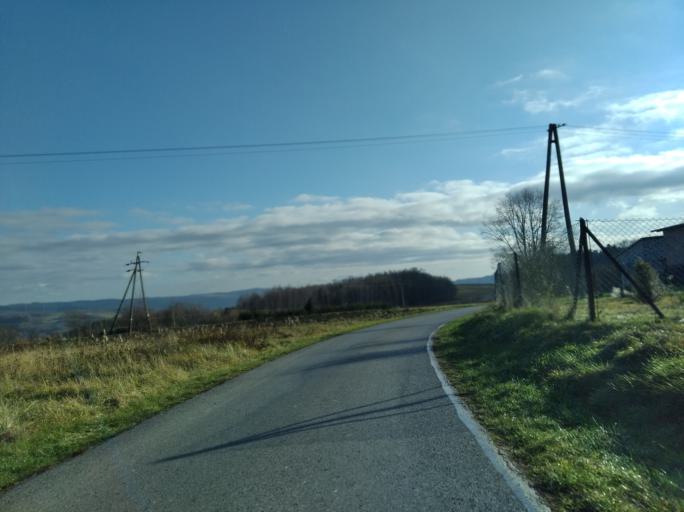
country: PL
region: Subcarpathian Voivodeship
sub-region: Powiat strzyzowski
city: Czudec
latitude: 49.9143
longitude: 21.8458
